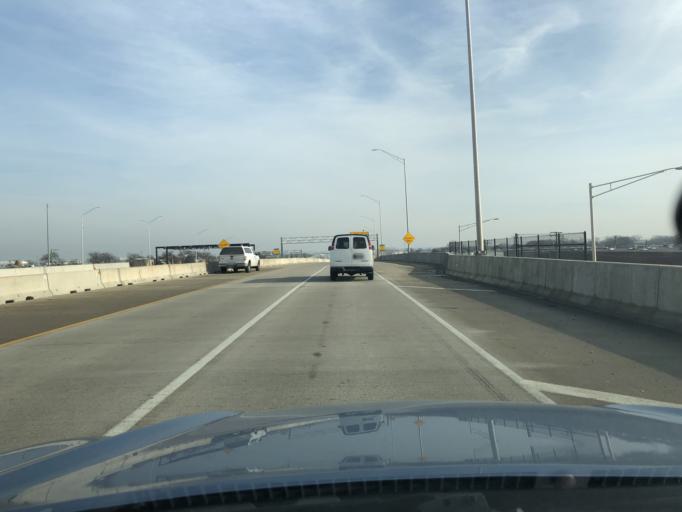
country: US
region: Illinois
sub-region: Cook County
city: Elk Grove Village
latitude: 41.9831
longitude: -87.9706
